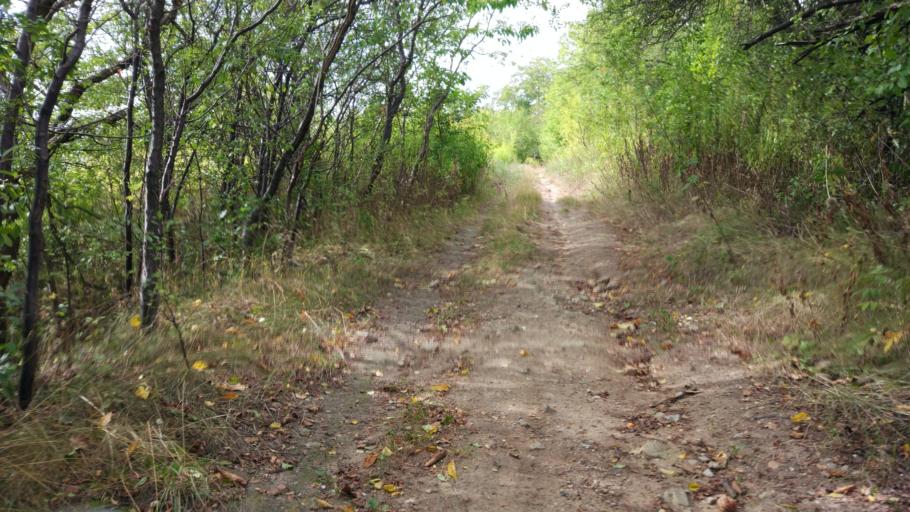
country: PL
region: Masovian Voivodeship
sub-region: Plock
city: Plock
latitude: 52.5273
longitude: 19.7465
